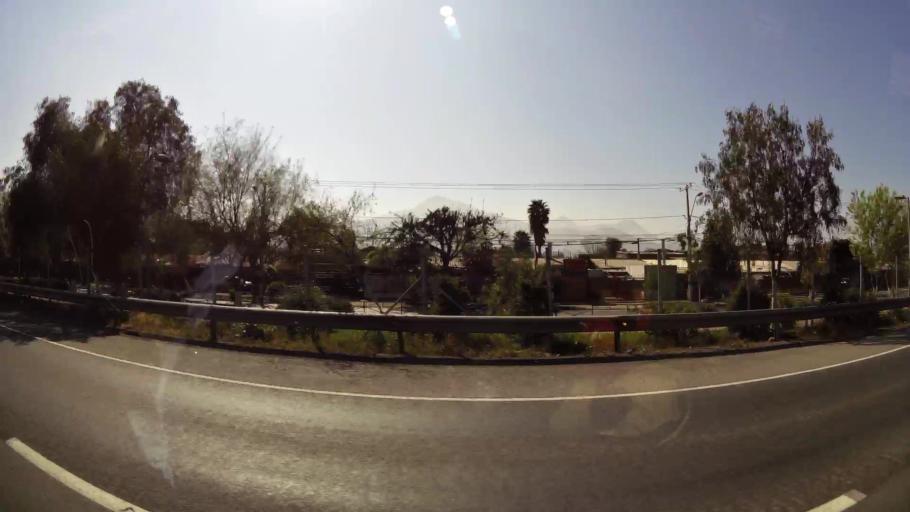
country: CL
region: Santiago Metropolitan
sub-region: Provincia de Chacabuco
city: Chicureo Abajo
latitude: -33.3589
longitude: -70.6910
